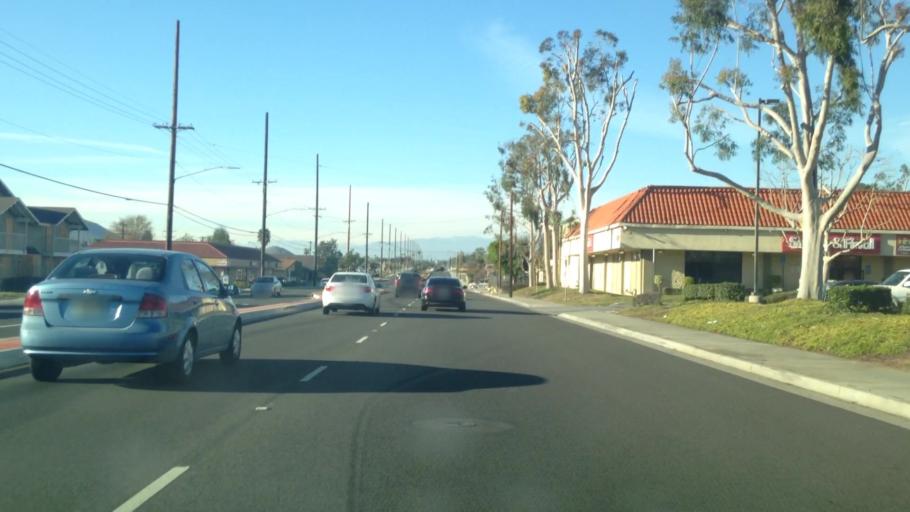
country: US
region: California
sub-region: Riverside County
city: Pedley
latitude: 33.9161
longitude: -117.4647
